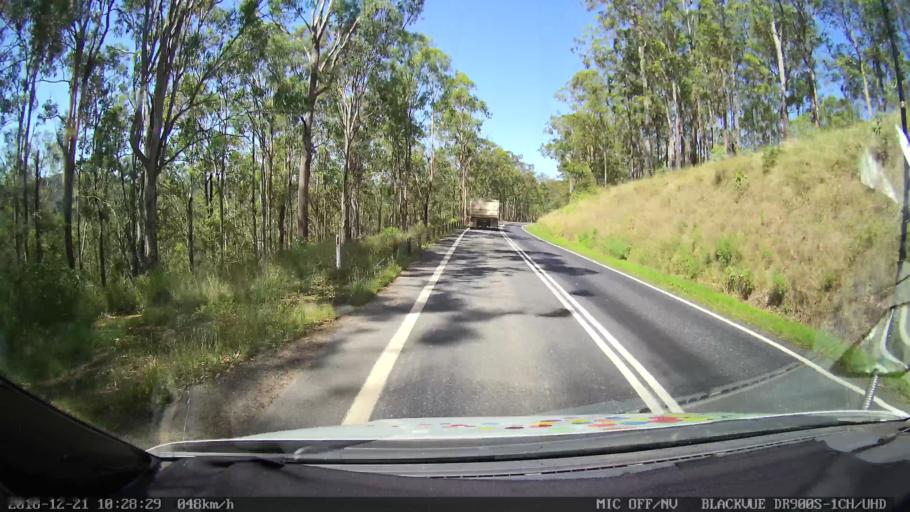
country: AU
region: New South Wales
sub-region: Clarence Valley
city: South Grafton
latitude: -29.6312
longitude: 152.7341
